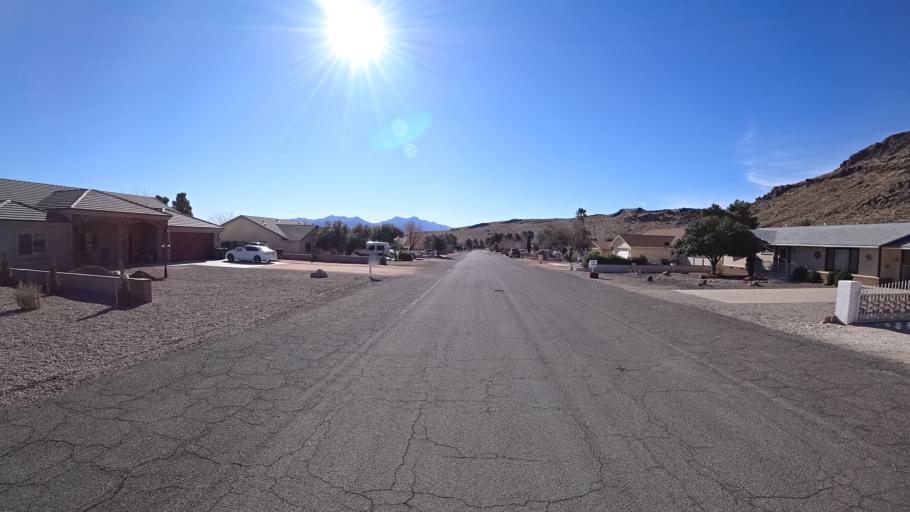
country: US
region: Arizona
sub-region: Mohave County
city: New Kingman-Butler
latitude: 35.2627
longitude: -114.0462
